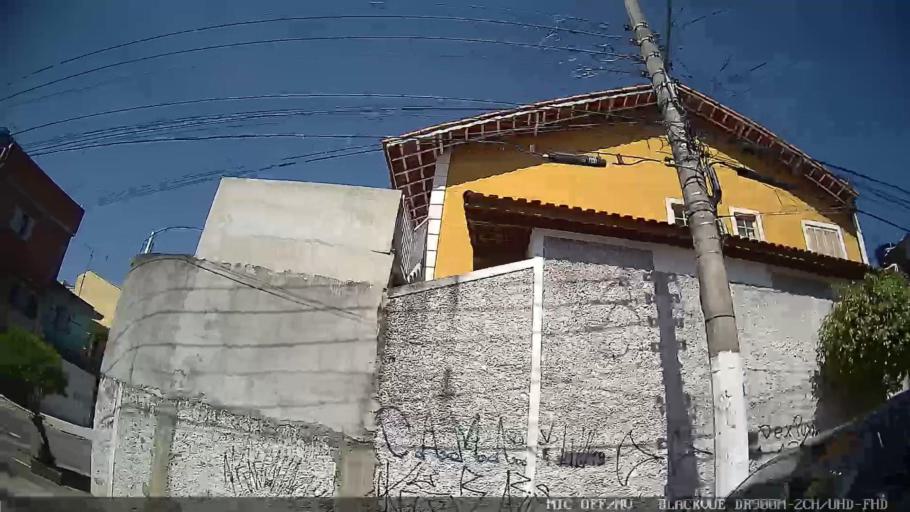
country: BR
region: Sao Paulo
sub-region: Sao Caetano Do Sul
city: Sao Caetano do Sul
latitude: -23.5934
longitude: -46.4997
